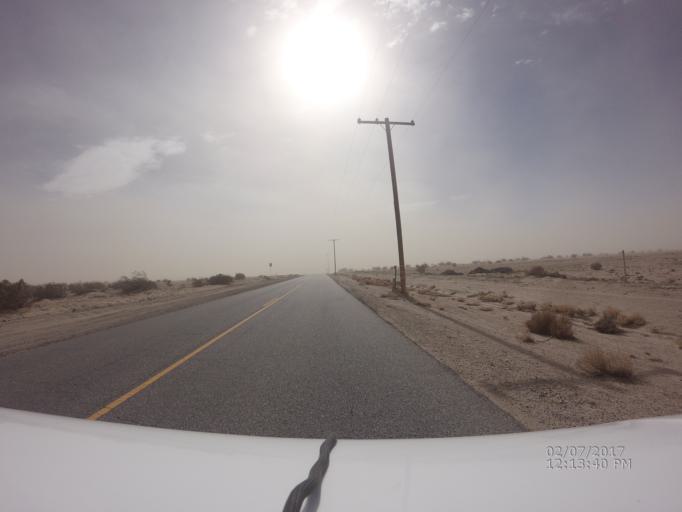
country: US
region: California
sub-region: Los Angeles County
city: Lake Los Angeles
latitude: 34.6550
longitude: -117.8275
